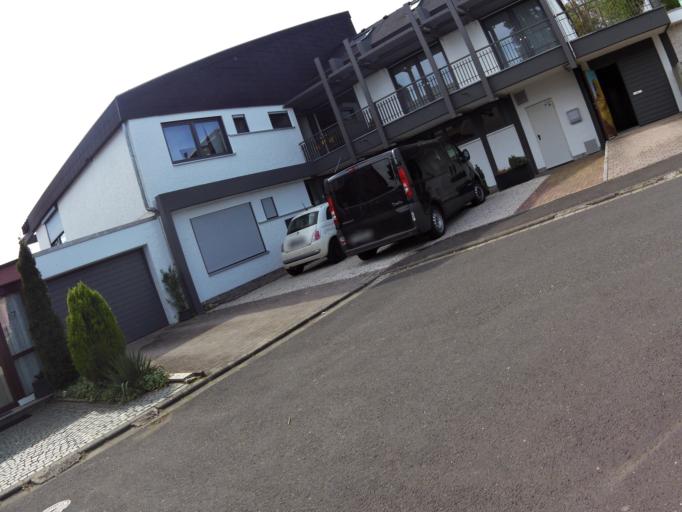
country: DE
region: Bavaria
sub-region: Regierungsbezirk Unterfranken
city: Unterpleichfeld
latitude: 49.8676
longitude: 10.0362
